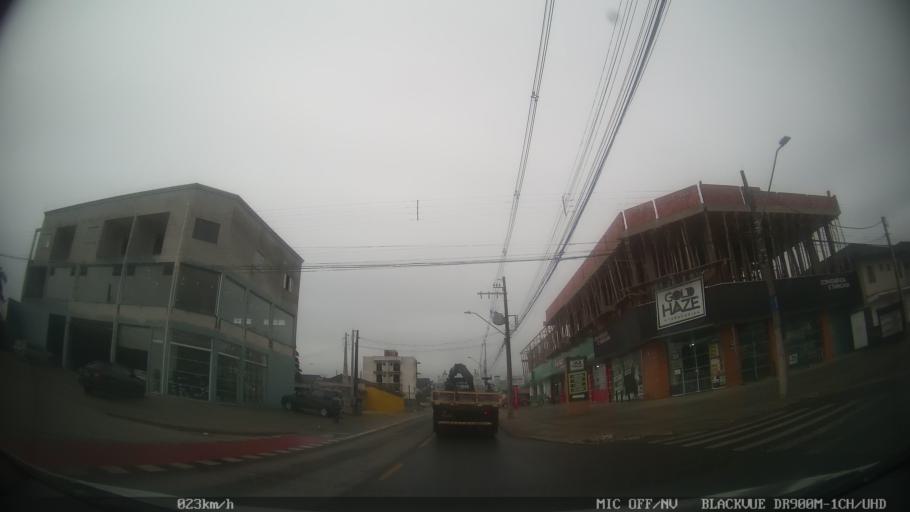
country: BR
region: Santa Catarina
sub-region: Joinville
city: Joinville
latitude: -26.2453
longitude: -48.8116
